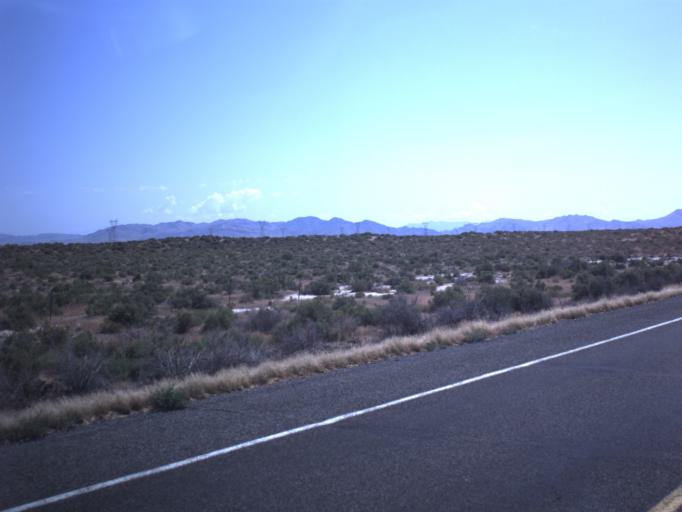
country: US
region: Utah
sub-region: Millard County
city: Delta
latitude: 39.4848
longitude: -112.5304
